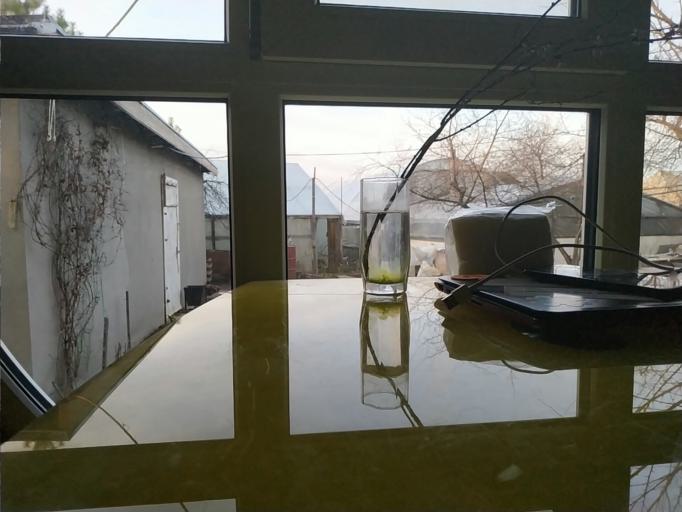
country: RU
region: Republic of Karelia
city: Suoyarvi
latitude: 62.3676
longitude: 32.0417
